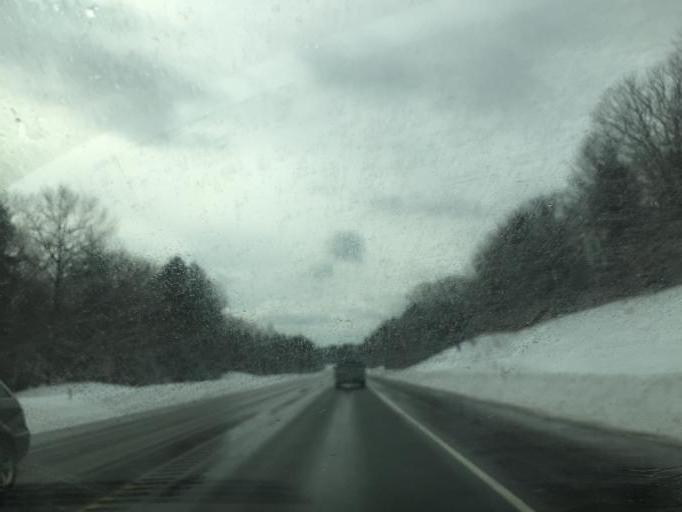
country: US
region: New Hampshire
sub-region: Carroll County
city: Sanbornville
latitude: 43.5085
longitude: -71.0290
